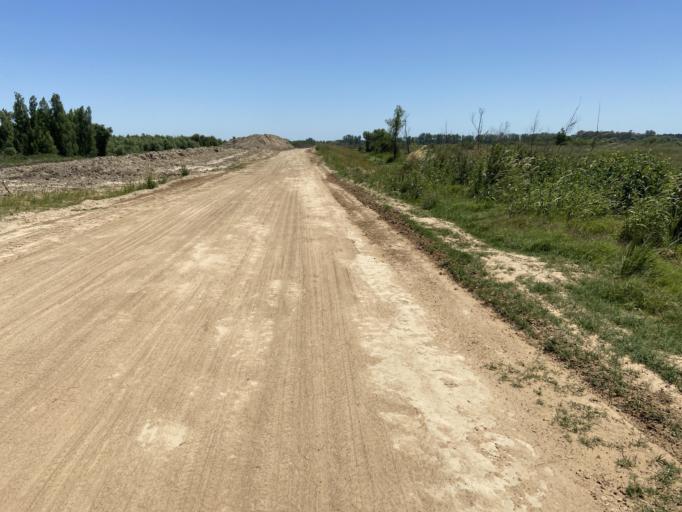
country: AR
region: Entre Rios
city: Villa Paranacito
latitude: -33.7115
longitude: -58.6502
